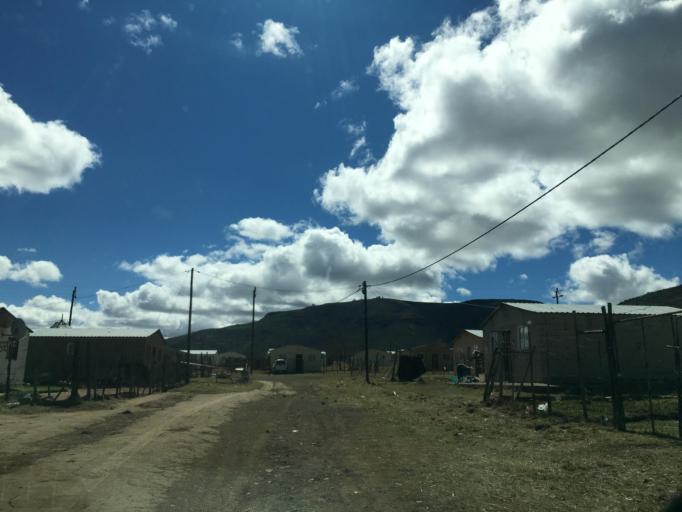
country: ZA
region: Eastern Cape
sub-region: Chris Hani District Municipality
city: Cala
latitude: -31.5429
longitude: 27.6986
